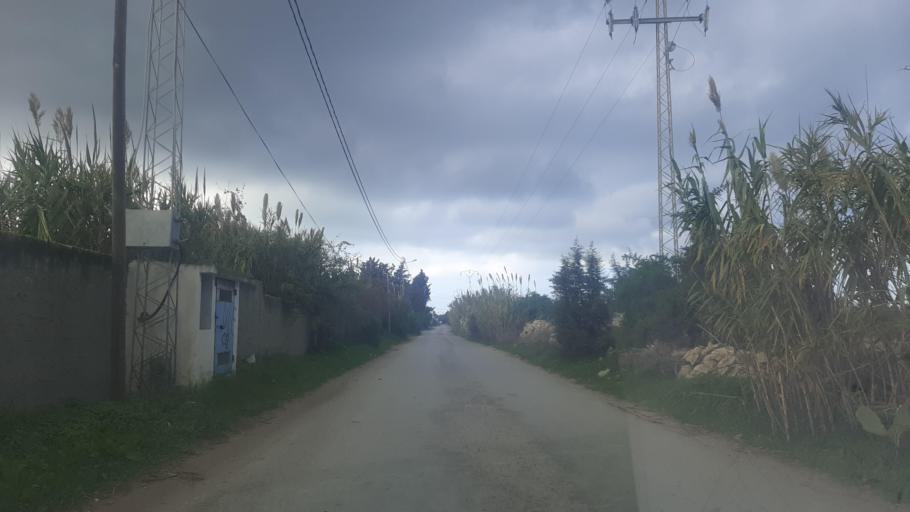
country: TN
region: Nabul
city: Manzil Bu Zalafah
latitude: 36.7308
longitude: 10.5392
